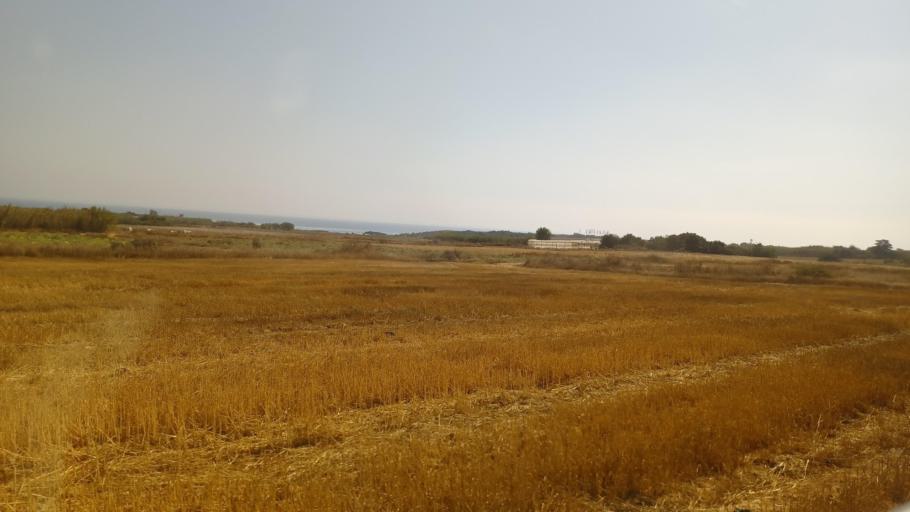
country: CY
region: Ammochostos
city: Paralimni
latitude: 35.0635
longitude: 33.9937
